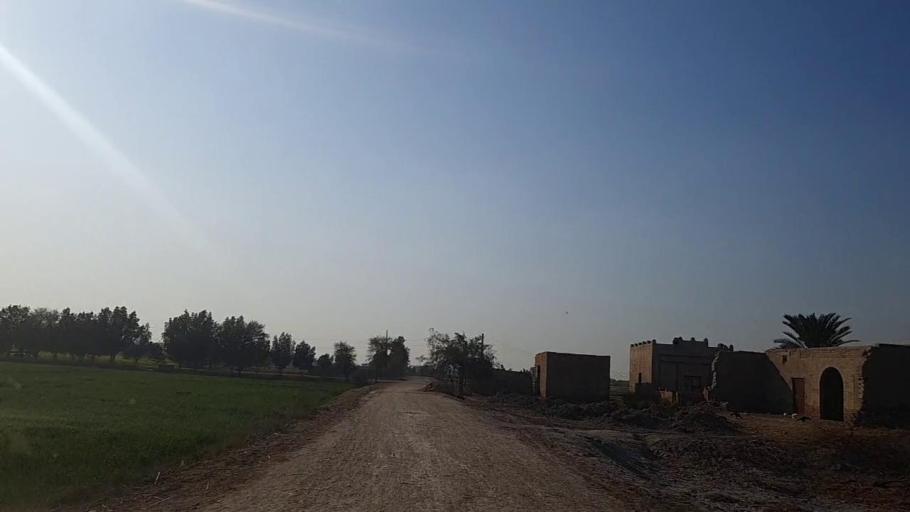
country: PK
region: Sindh
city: Daur
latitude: 26.3296
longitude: 68.1717
